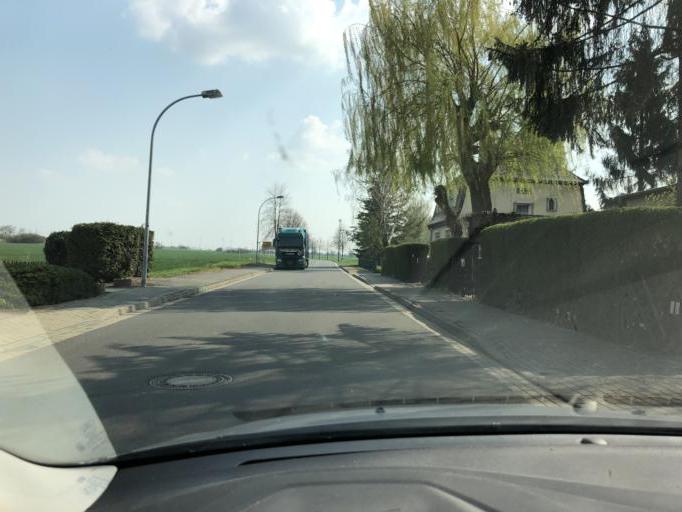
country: DE
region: Saxony-Anhalt
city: Radegast
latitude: 51.6130
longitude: 12.0653
